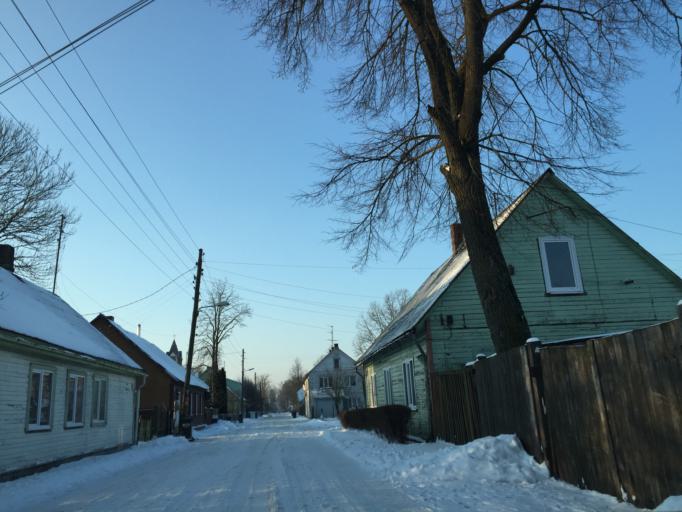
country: LV
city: Tireli
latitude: 56.9442
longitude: 23.6212
